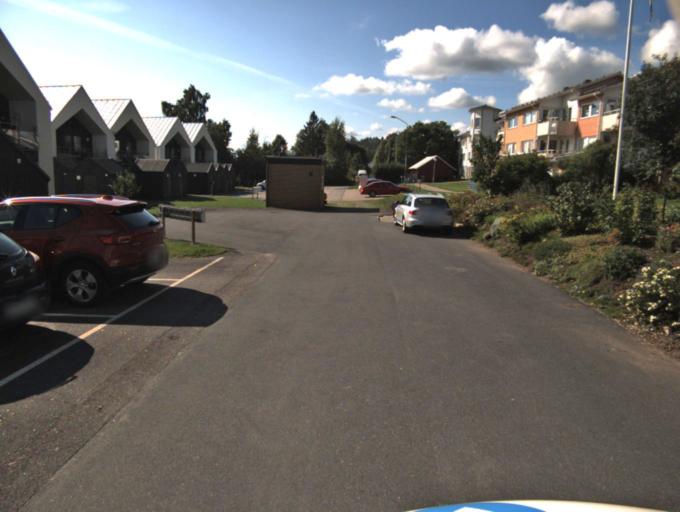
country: SE
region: Vaestra Goetaland
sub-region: Ulricehamns Kommun
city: Ulricehamn
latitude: 57.7995
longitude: 13.3968
